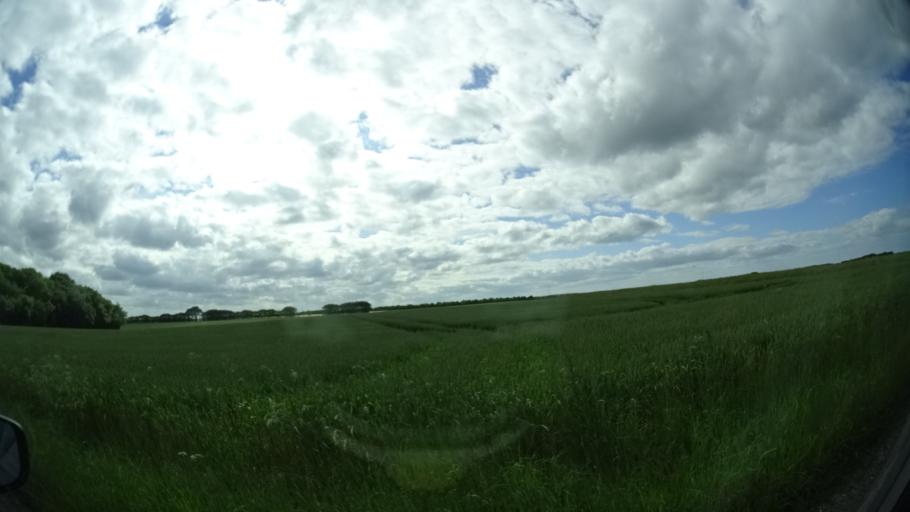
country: DK
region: Central Jutland
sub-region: Norddjurs Kommune
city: Grenaa
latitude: 56.4603
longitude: 10.7132
